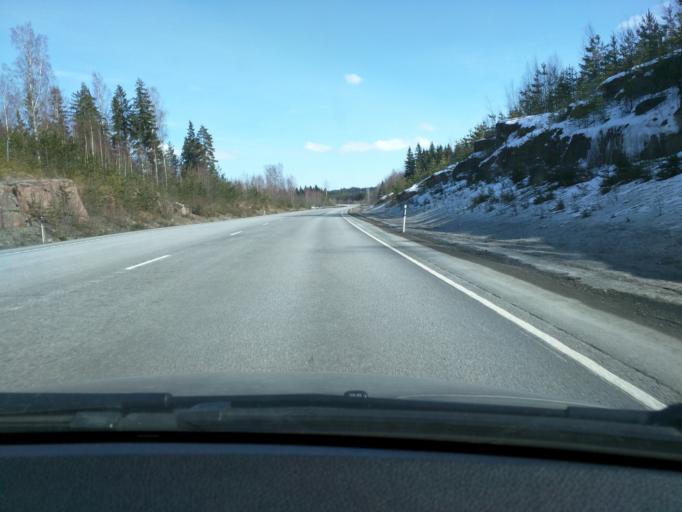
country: FI
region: Uusimaa
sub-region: Loviisa
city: Liljendal
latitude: 60.5286
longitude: 25.9770
